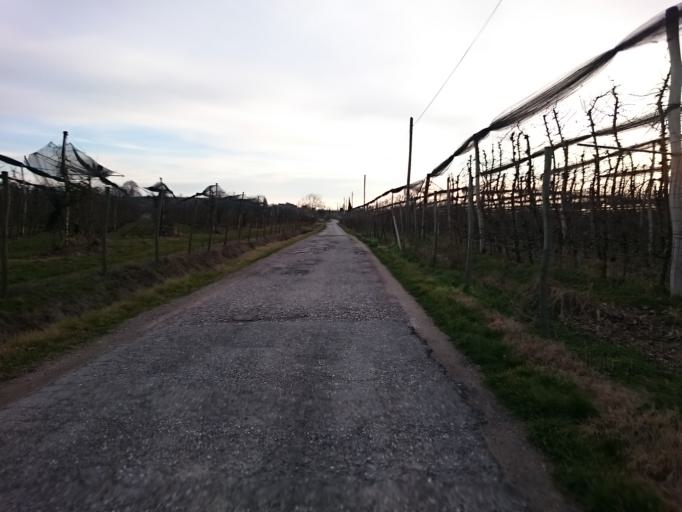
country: IT
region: Veneto
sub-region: Provincia di Verona
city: Castelnuovo del Garda
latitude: 45.4541
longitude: 10.7545
